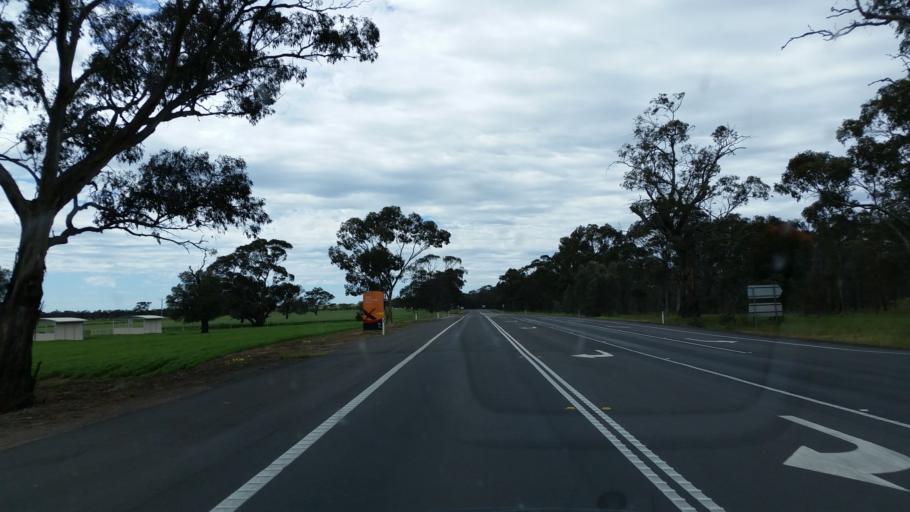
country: AU
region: South Australia
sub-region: Tatiara
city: Bordertown
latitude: -36.3443
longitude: 140.9684
